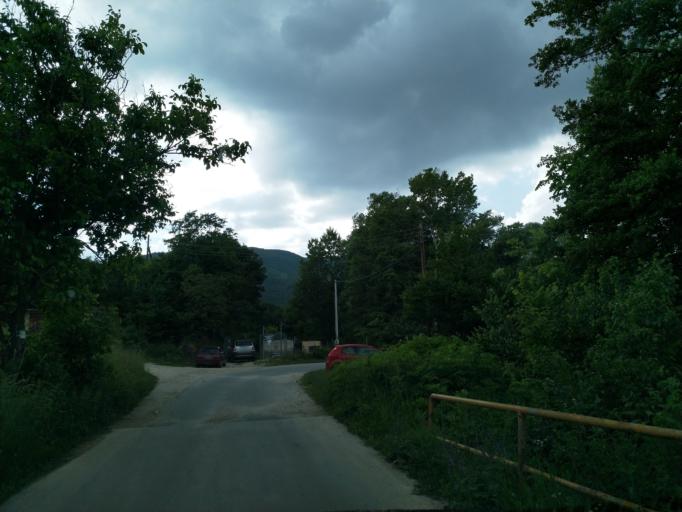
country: RS
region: Central Serbia
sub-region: Borski Okrug
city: Bor
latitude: 44.0281
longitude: 21.9684
